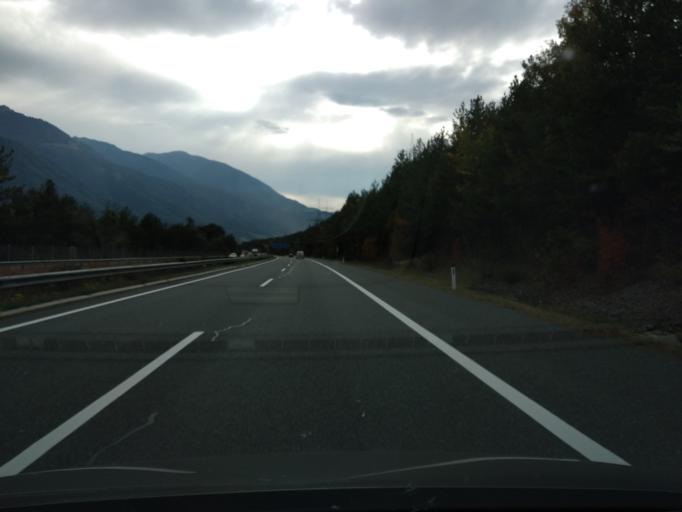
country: AT
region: Tyrol
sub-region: Politischer Bezirk Imst
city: Haiming
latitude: 47.2450
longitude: 10.8520
